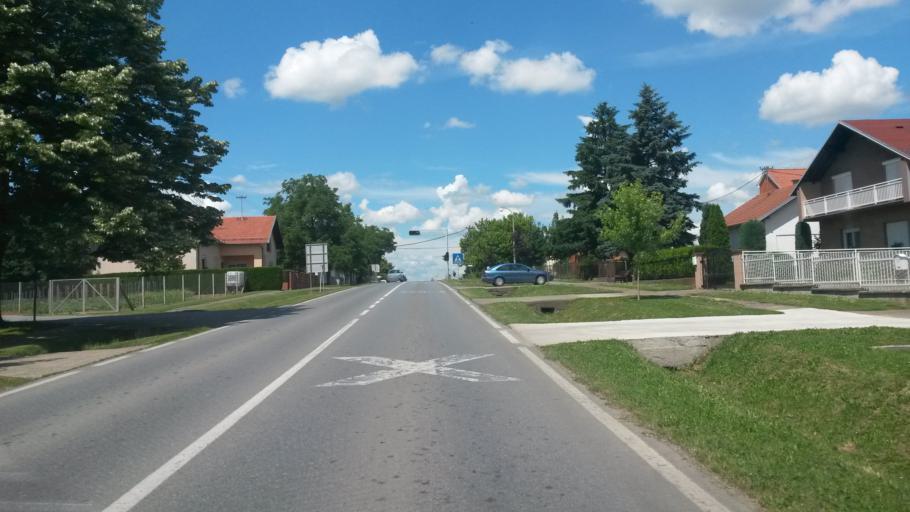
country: HR
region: Osjecko-Baranjska
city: Viskovci
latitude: 45.3473
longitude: 18.4222
